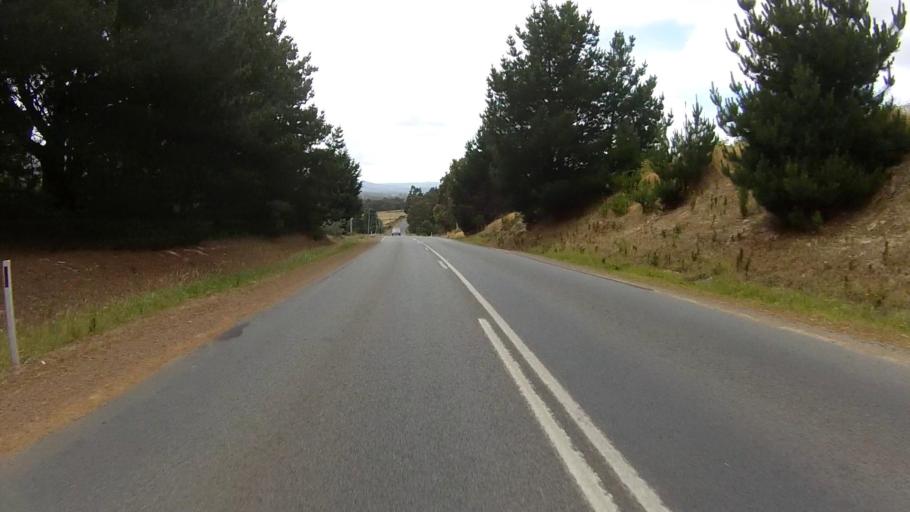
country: AU
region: Tasmania
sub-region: Kingborough
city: Kettering
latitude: -43.0894
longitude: 147.2504
